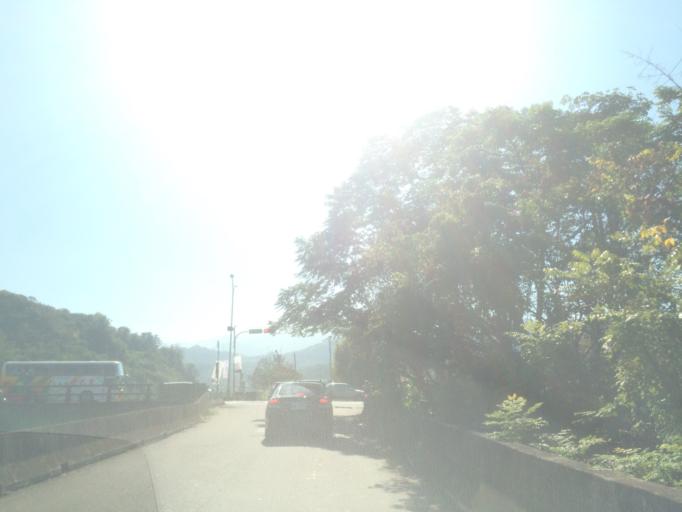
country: TW
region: Taiwan
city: Lugu
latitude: 23.7768
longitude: 120.7103
